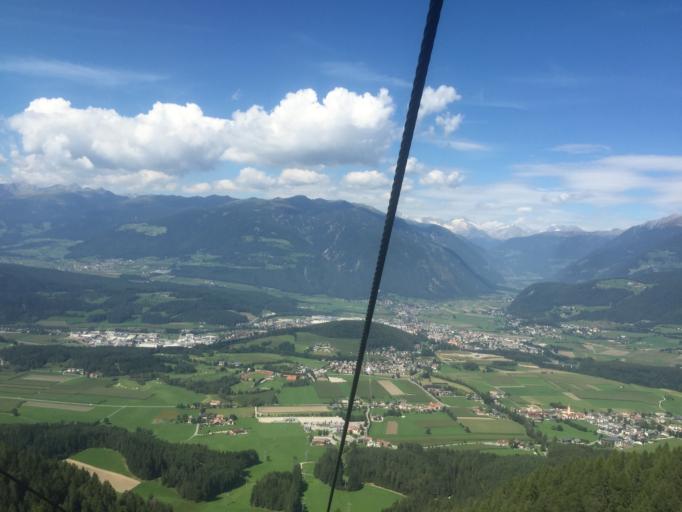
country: IT
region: Trentino-Alto Adige
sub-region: Bolzano
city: Riscone
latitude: 46.7580
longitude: 11.9477
